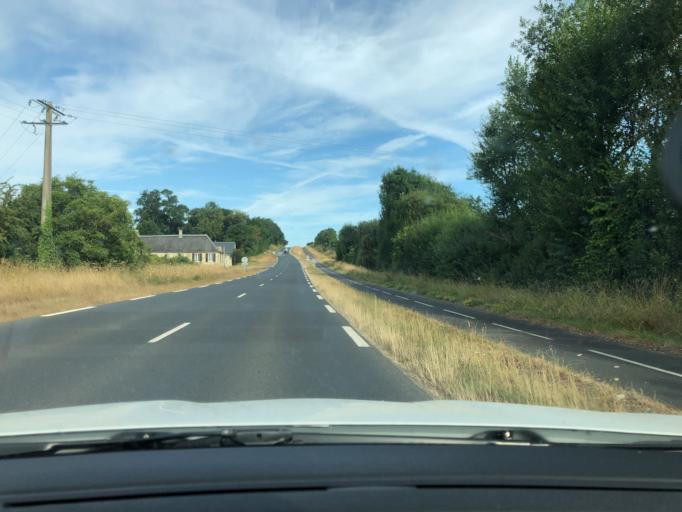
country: FR
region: Lower Normandy
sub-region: Departement du Calvados
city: Saint-Vigor-le-Grand
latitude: 49.2518
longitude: -0.6338
